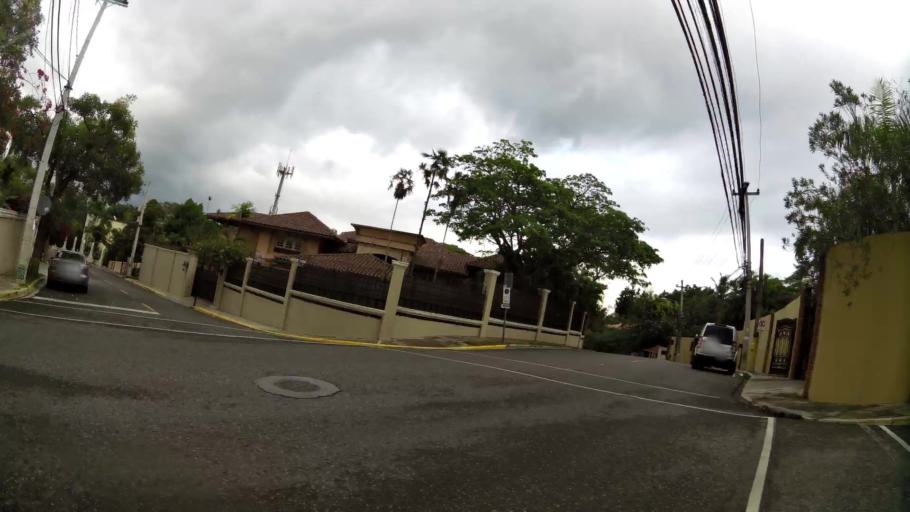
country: DO
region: Nacional
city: La Agustina
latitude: 18.5102
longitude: -69.9437
